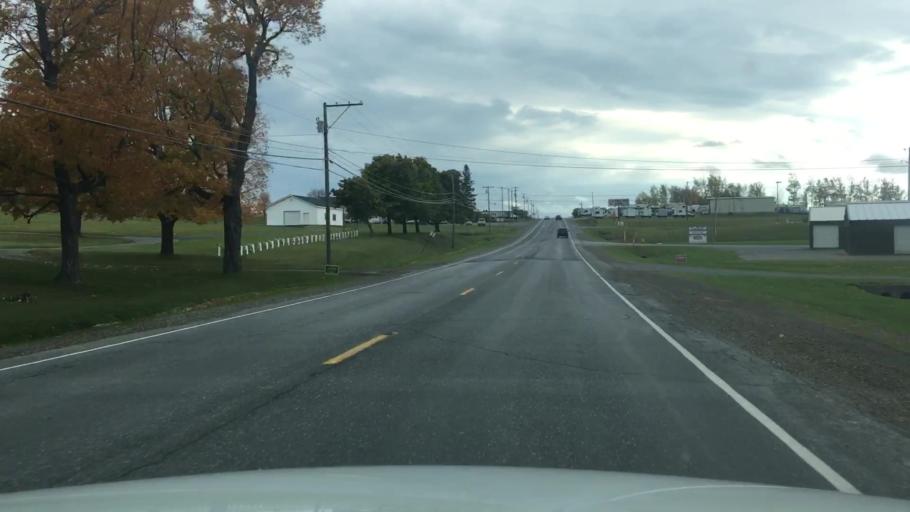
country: US
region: Maine
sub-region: Aroostook County
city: Presque Isle
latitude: 46.6629
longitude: -68.0092
